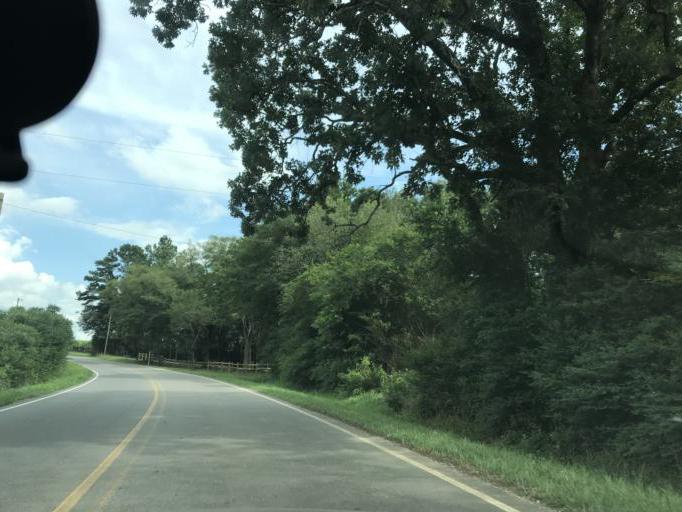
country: US
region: Georgia
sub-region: Cherokee County
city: Ball Ground
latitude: 34.3140
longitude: -84.2413
